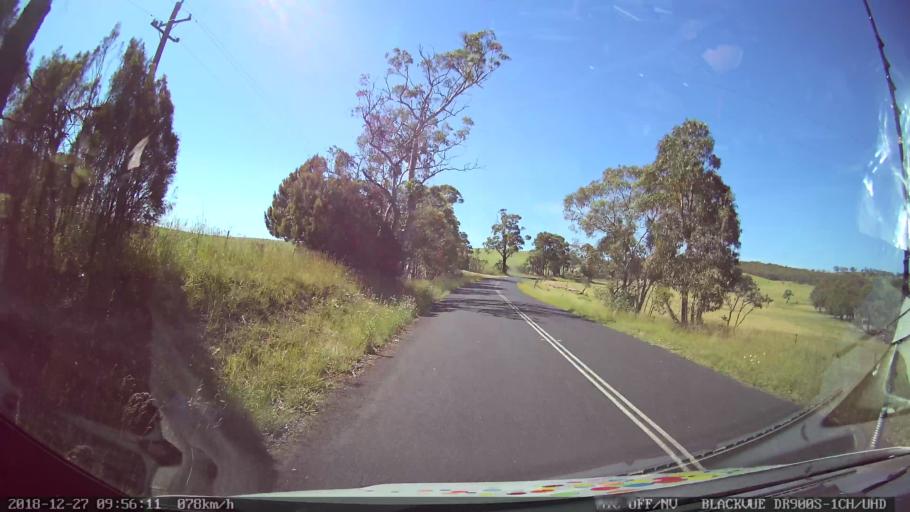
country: AU
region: New South Wales
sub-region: Lithgow
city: Portland
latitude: -33.4096
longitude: 149.9720
